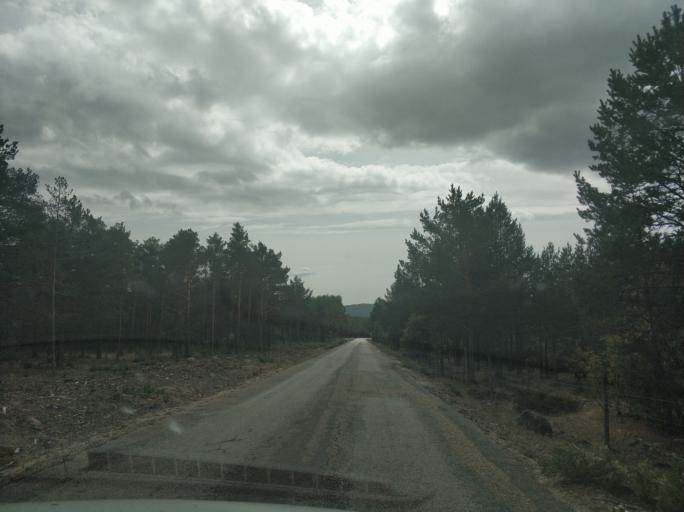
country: ES
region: Castille and Leon
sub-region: Provincia de Soria
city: Duruelo de la Sierra
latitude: 41.9599
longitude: -2.9200
